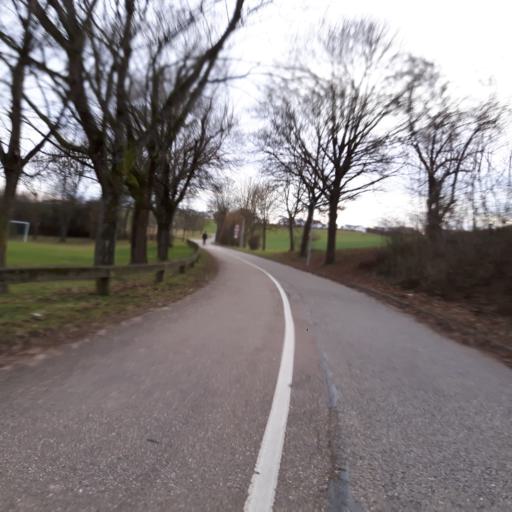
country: DE
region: Baden-Wuerttemberg
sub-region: Regierungsbezirk Stuttgart
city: Steinheim am der Murr
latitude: 48.9784
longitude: 9.2852
